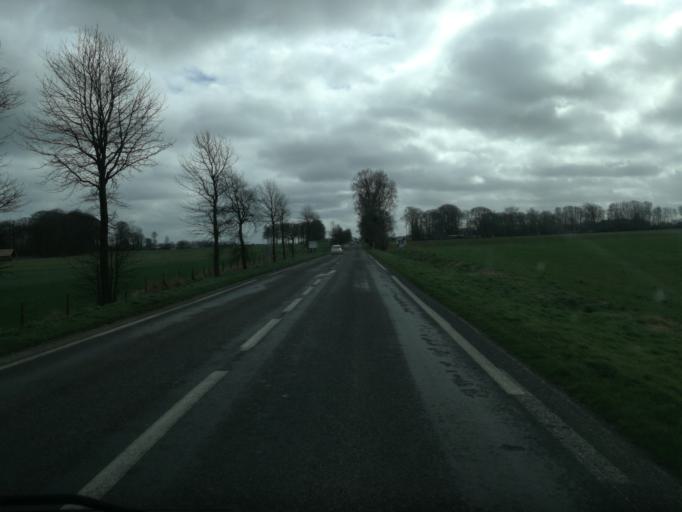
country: FR
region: Haute-Normandie
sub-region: Departement de la Seine-Maritime
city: Valliquerville
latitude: 49.6221
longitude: 0.6511
